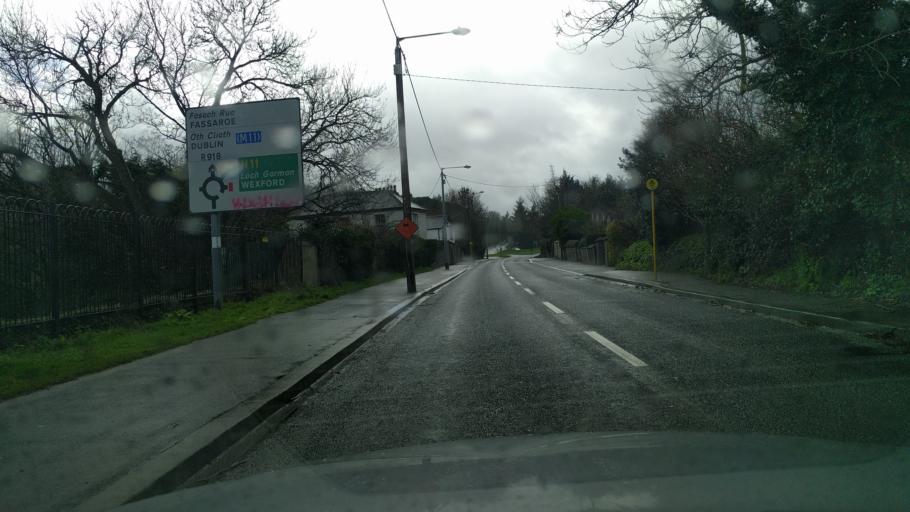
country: IE
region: Leinster
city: Little Bray
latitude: 53.1990
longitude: -6.1303
